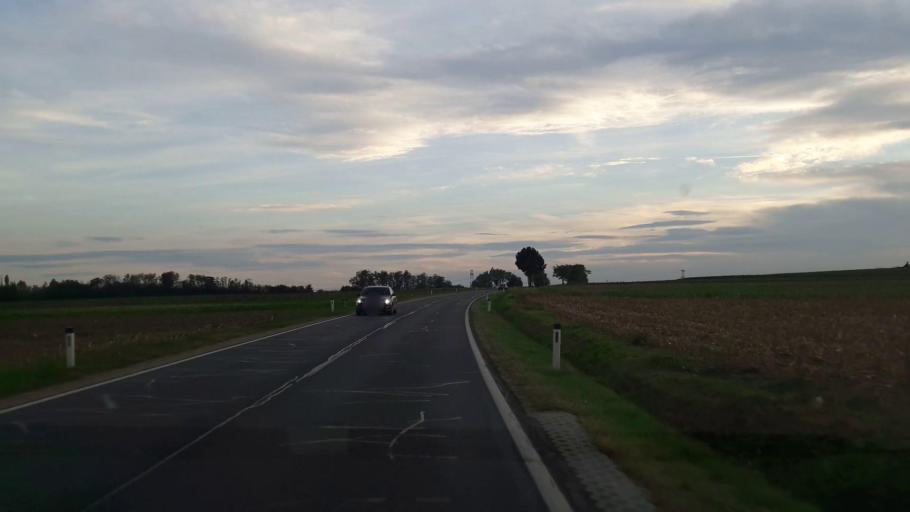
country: AT
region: Lower Austria
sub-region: Politischer Bezirk Korneuburg
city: Harmannsdorf
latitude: 48.3730
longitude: 16.3605
